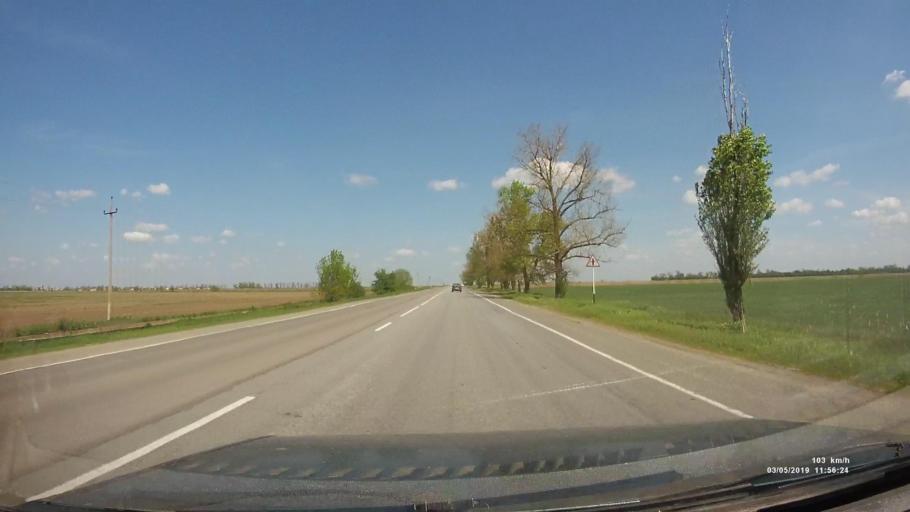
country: RU
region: Rostov
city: Bagayevskaya
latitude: 47.1942
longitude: 40.3007
